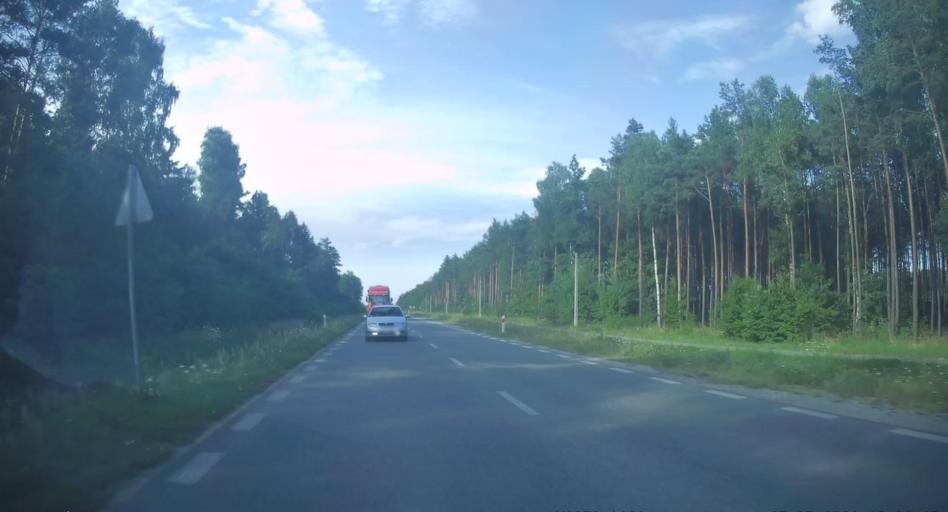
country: PL
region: Swietokrzyskie
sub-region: Powiat konecki
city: Konskie
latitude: 51.1242
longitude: 20.3565
